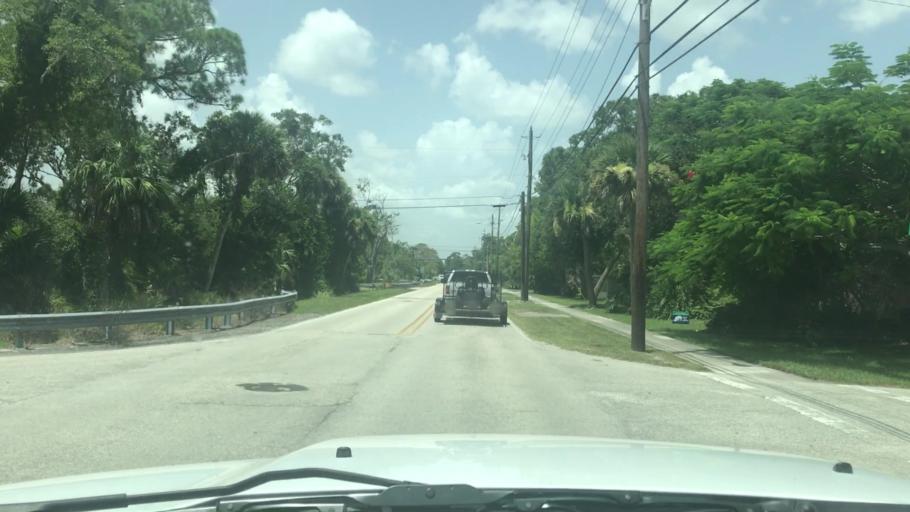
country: US
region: Florida
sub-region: Indian River County
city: Vero Beach South
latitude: 27.6310
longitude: -80.4111
